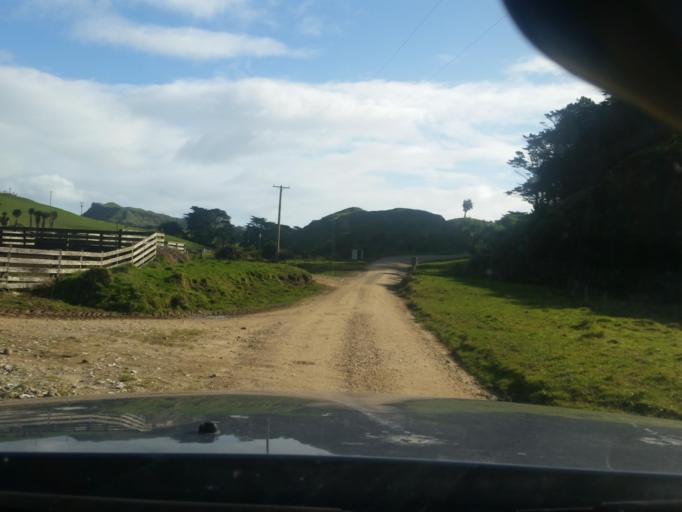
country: NZ
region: Tasman
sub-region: Tasman District
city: Takaka
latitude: -40.5548
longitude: 172.6169
